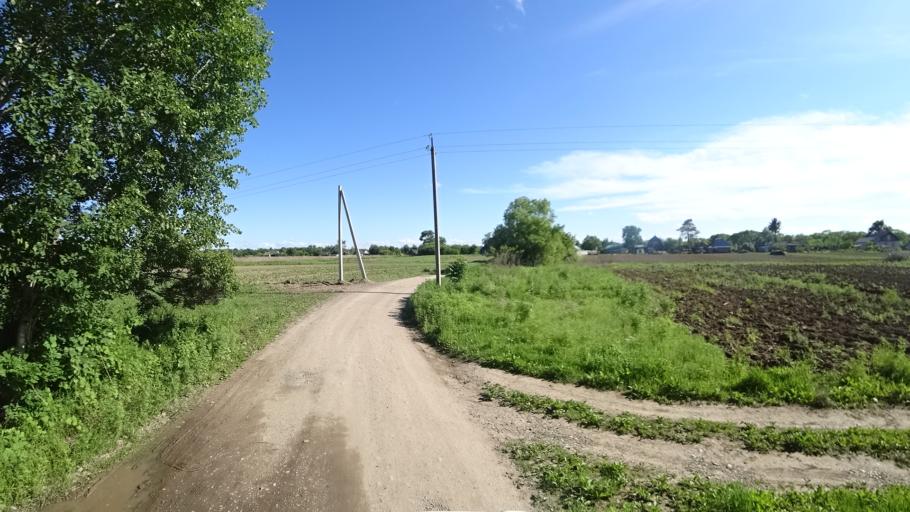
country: RU
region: Khabarovsk Krai
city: Khor
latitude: 47.8869
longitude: 135.0194
